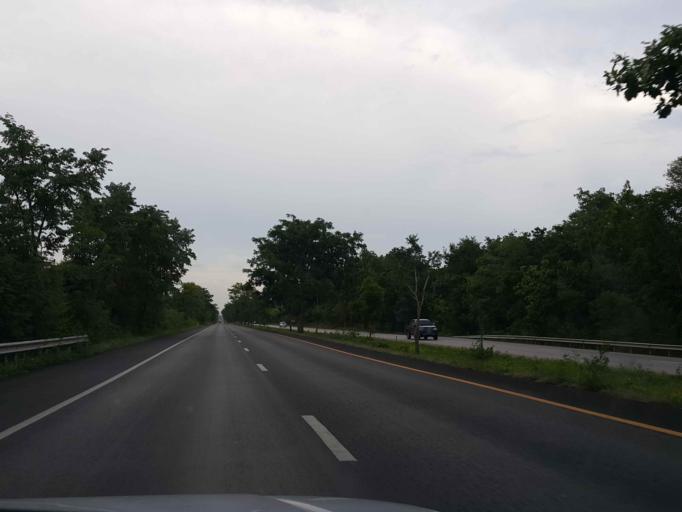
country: TH
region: Lampang
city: Ko Kha
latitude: 18.0772
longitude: 99.3931
